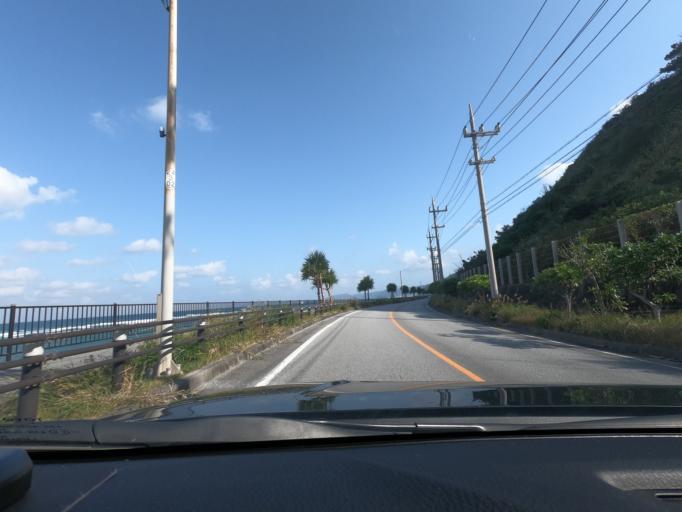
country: JP
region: Okinawa
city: Nago
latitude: 26.7607
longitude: 128.1898
